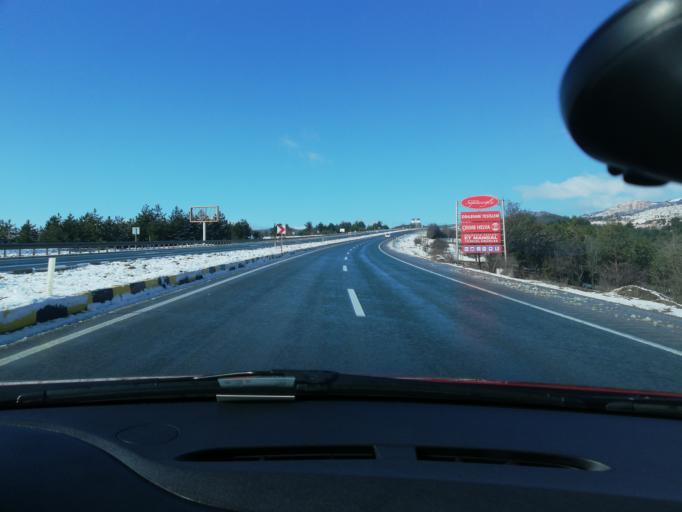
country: TR
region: Kastamonu
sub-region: Cide
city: Kastamonu
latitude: 41.3648
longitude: 33.7394
